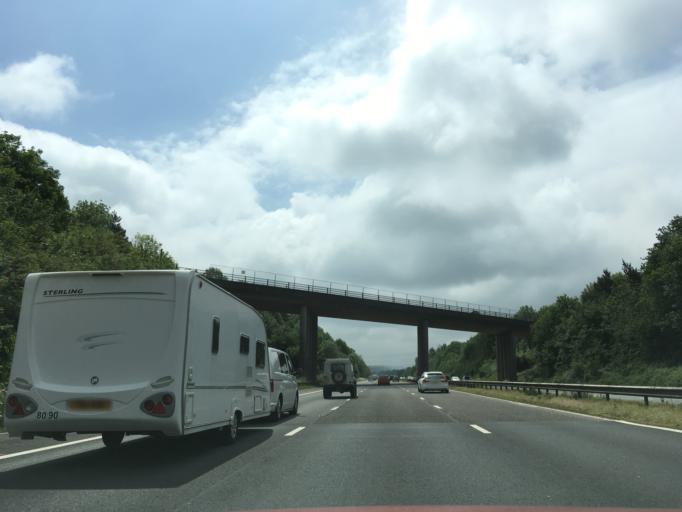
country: GB
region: England
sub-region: Devon
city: Cullompton
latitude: 50.8819
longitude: -3.3801
